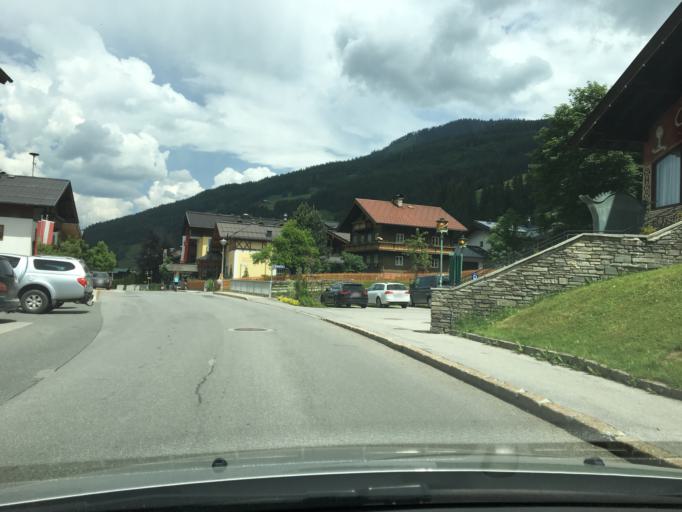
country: AT
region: Salzburg
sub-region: Politischer Bezirk Sankt Johann im Pongau
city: Kleinarl
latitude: 47.2773
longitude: 13.3196
